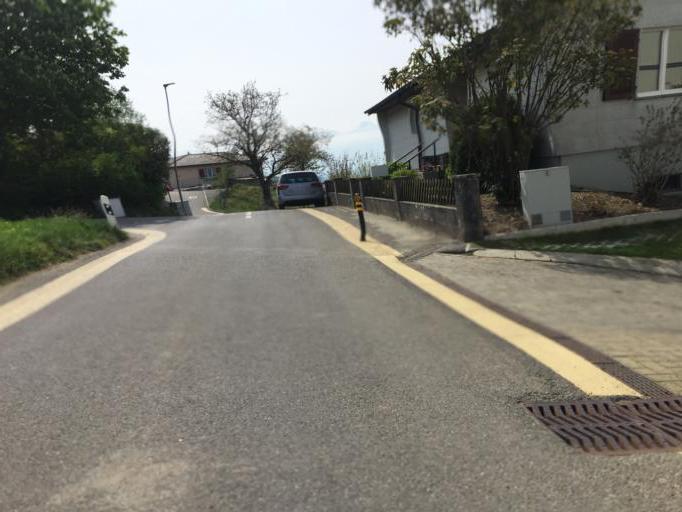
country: CH
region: Bern
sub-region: Bern-Mittelland District
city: Niederwichtrach
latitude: 46.8554
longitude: 7.5813
